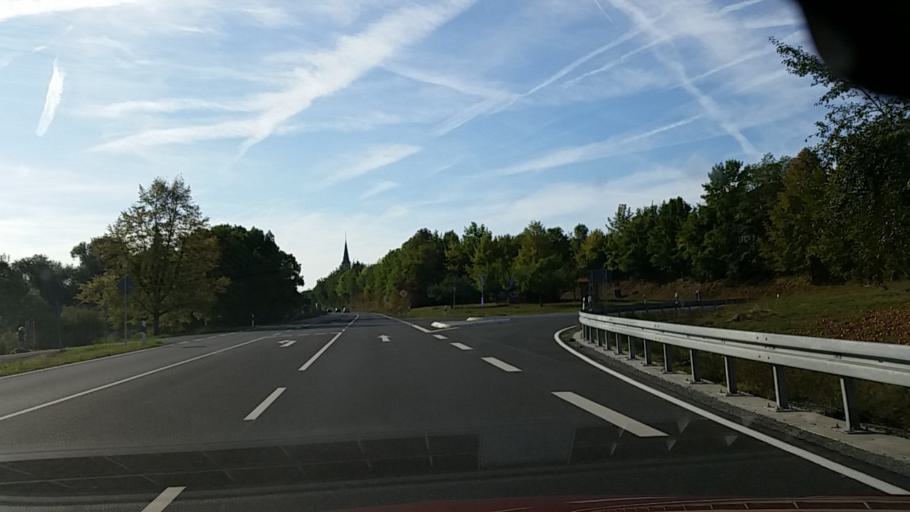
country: DE
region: Bavaria
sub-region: Regierungsbezirk Unterfranken
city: Erlabrunn
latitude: 49.8644
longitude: 9.8400
